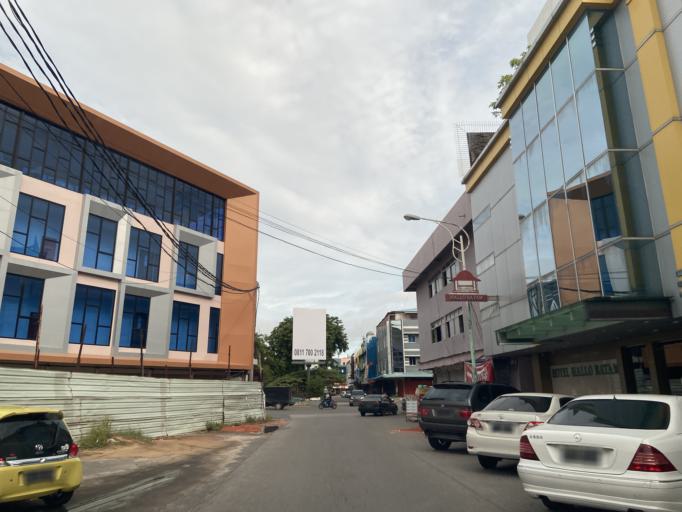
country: SG
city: Singapore
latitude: 1.1453
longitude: 104.0086
